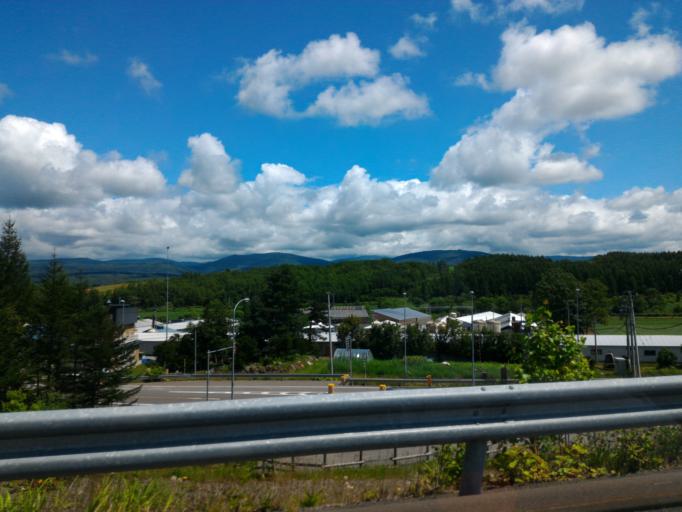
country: JP
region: Hokkaido
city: Nayoro
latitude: 44.4178
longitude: 142.4013
